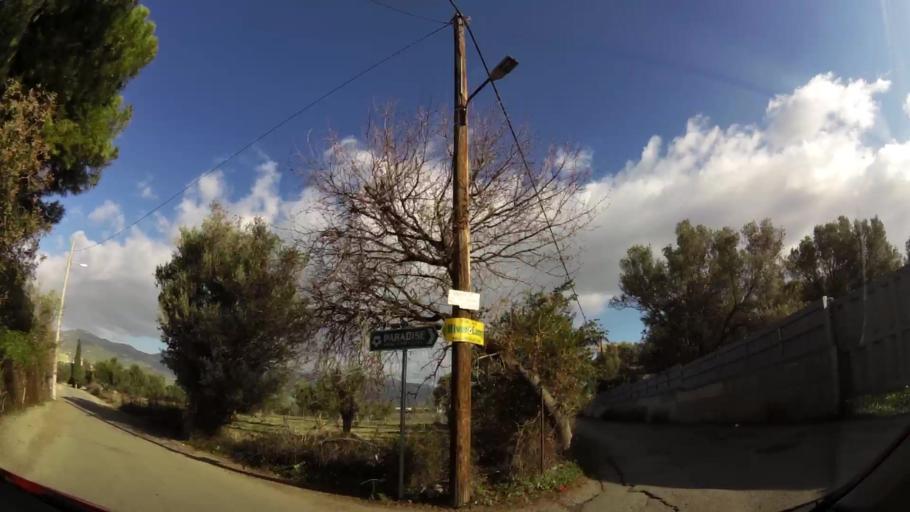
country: GR
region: Attica
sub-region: Nomarchia Athinas
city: Metamorfosi
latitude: 38.0725
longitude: 23.7516
